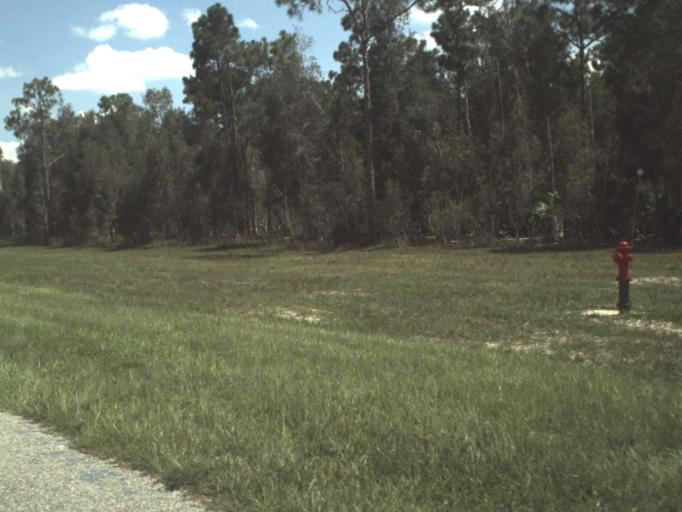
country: US
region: Florida
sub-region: Palm Beach County
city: Limestone Creek
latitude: 26.9002
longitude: -80.2855
